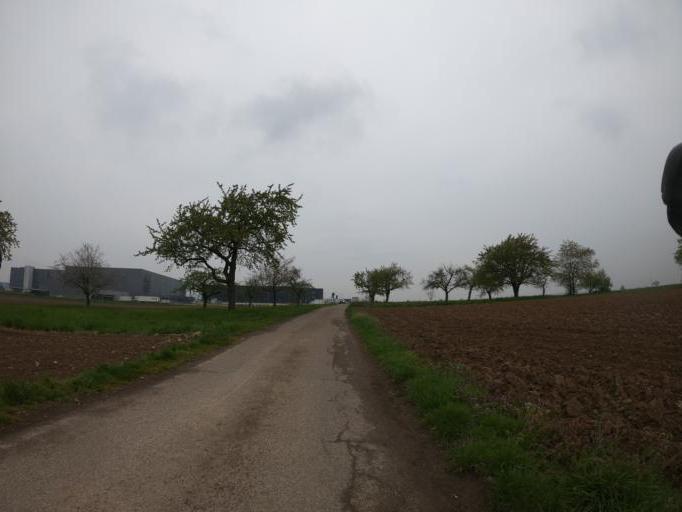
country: DE
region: Baden-Wuerttemberg
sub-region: Regierungsbezirk Stuttgart
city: Oberriexingen
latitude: 48.9463
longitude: 9.0543
